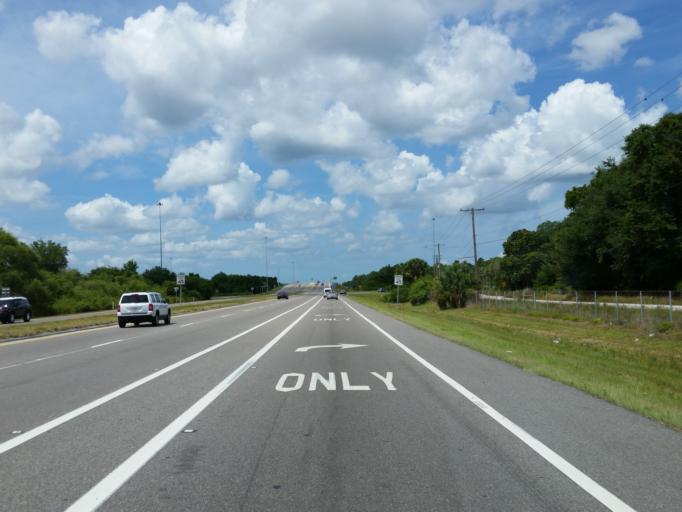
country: US
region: Florida
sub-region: Hillsborough County
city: Riverview
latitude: 27.8549
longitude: -82.3409
